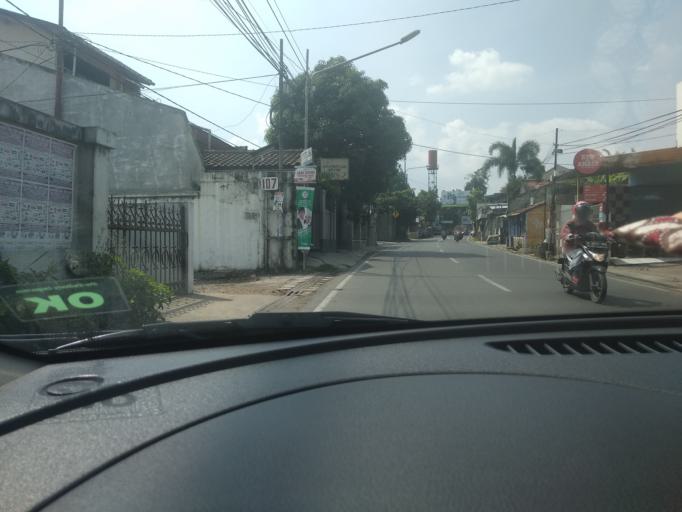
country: ID
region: West Java
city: Cimahi
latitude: -6.8898
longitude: 107.5640
